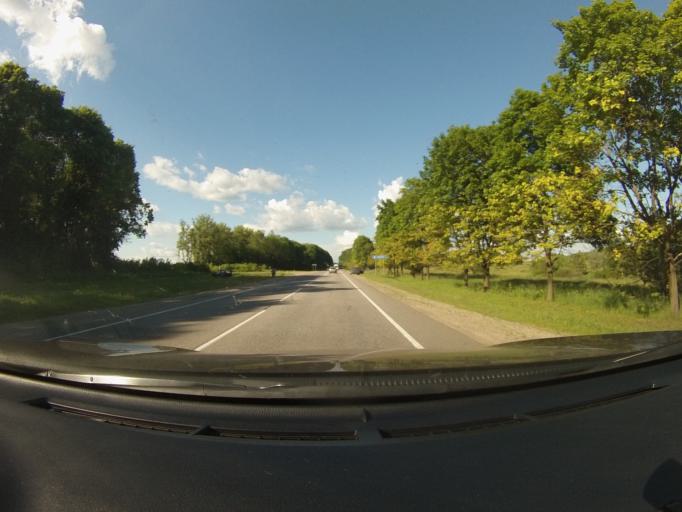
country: RU
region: Tula
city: Bol'shoye Skuratovo
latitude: 53.3857
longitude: 36.7457
